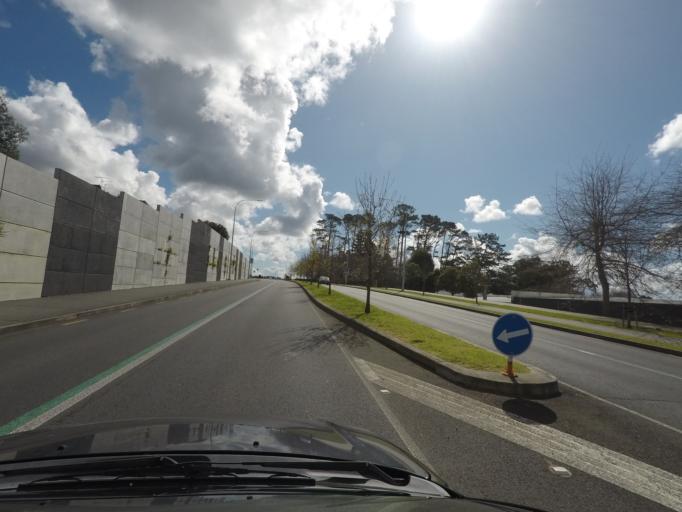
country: NZ
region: Auckland
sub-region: Auckland
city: Rothesay Bay
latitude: -36.7535
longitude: 174.6975
